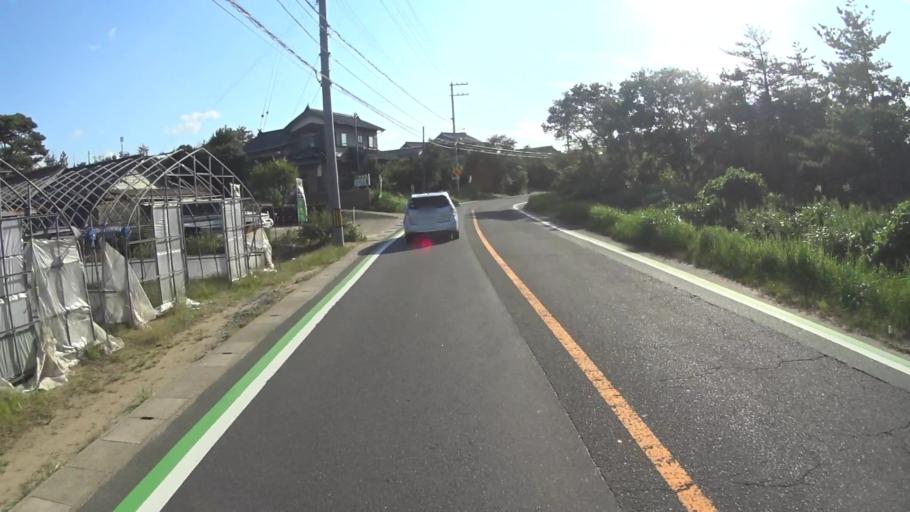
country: JP
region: Hyogo
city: Toyooka
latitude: 35.6560
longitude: 134.9569
